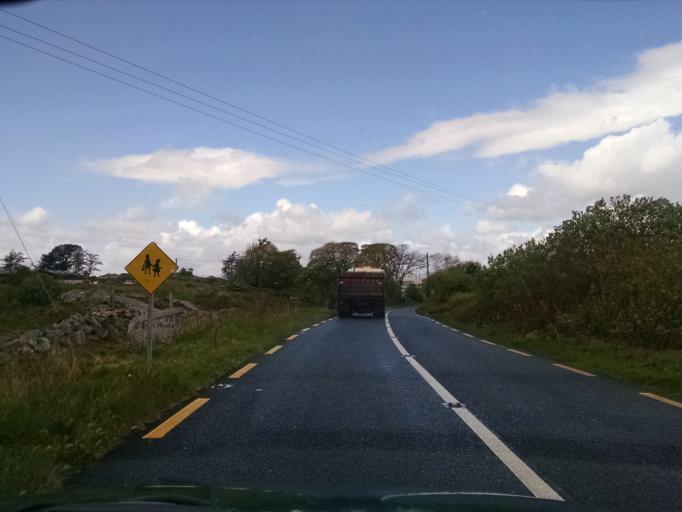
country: IE
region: Connaught
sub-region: County Galway
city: Oughterard
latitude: 53.3361
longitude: -9.5468
